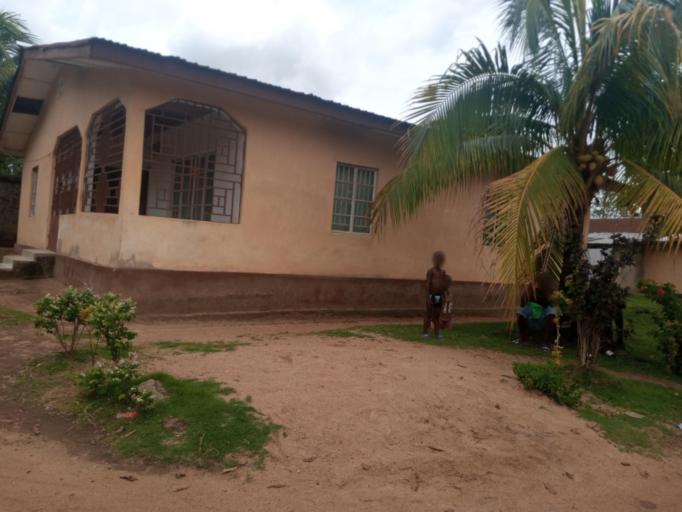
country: SL
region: Southern Province
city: Bo
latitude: 7.9573
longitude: -11.7168
